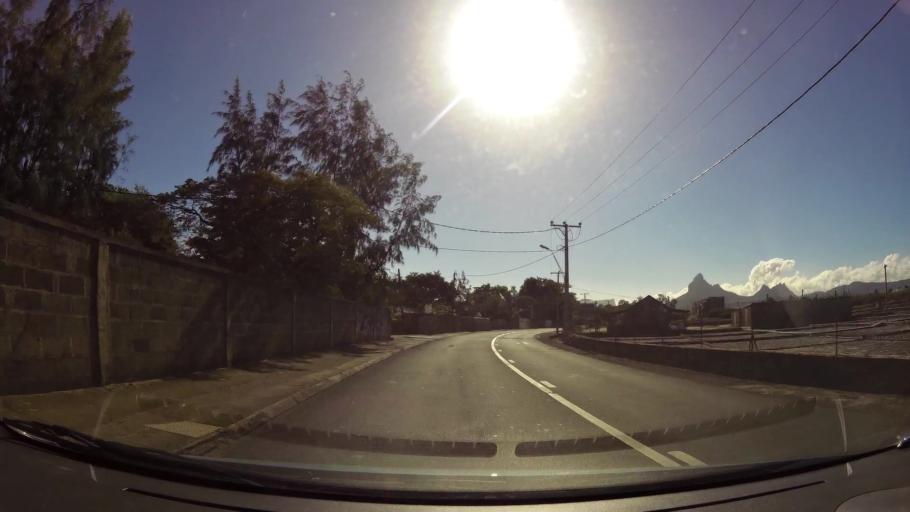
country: MU
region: Black River
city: Tamarin
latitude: -20.3338
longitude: 57.3670
